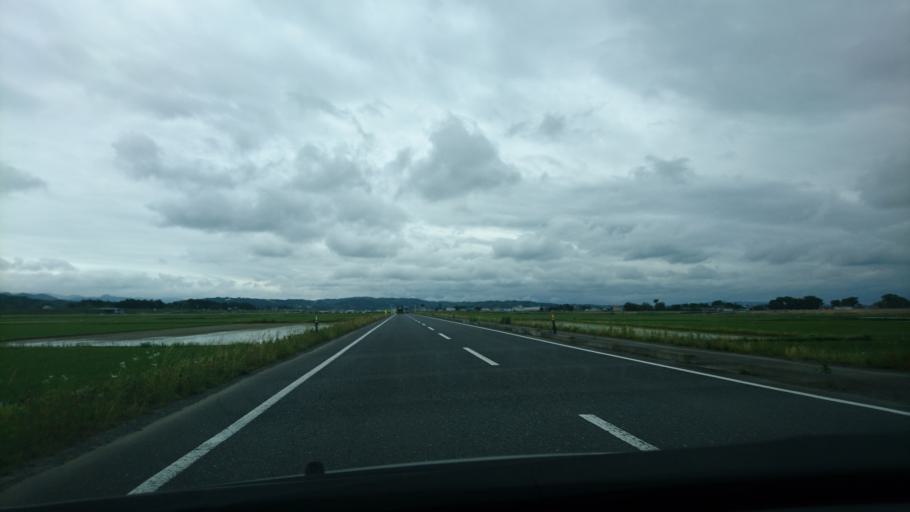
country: JP
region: Miyagi
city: Wakuya
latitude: 38.6837
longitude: 141.2610
